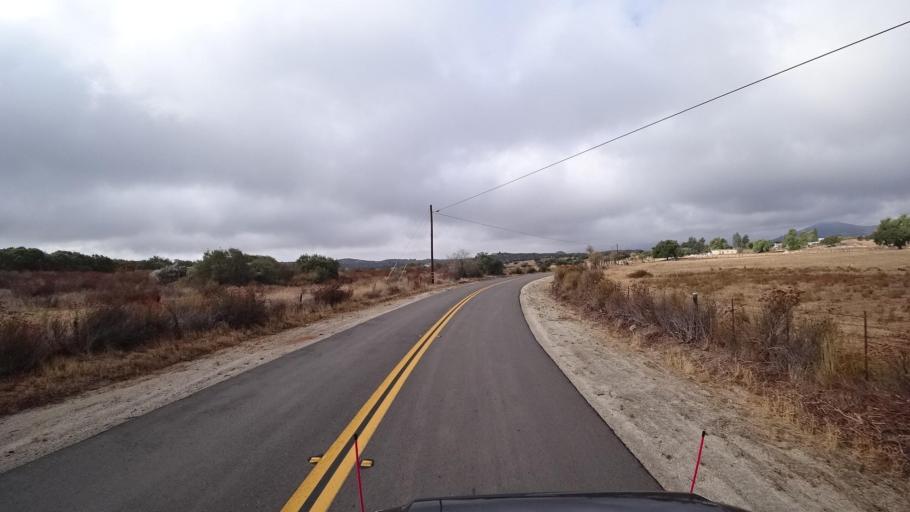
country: MX
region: Baja California
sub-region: Tecate
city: Hacienda Tecate
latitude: 32.6114
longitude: -116.5703
